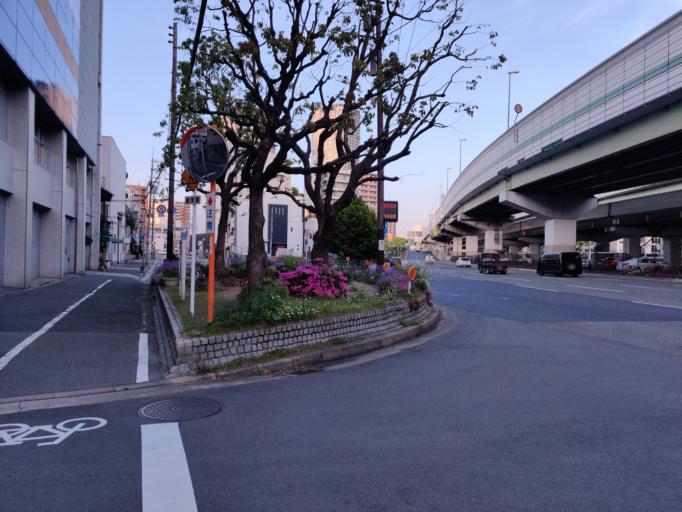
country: JP
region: Osaka
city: Osaka-shi
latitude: 34.6796
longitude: 135.4784
